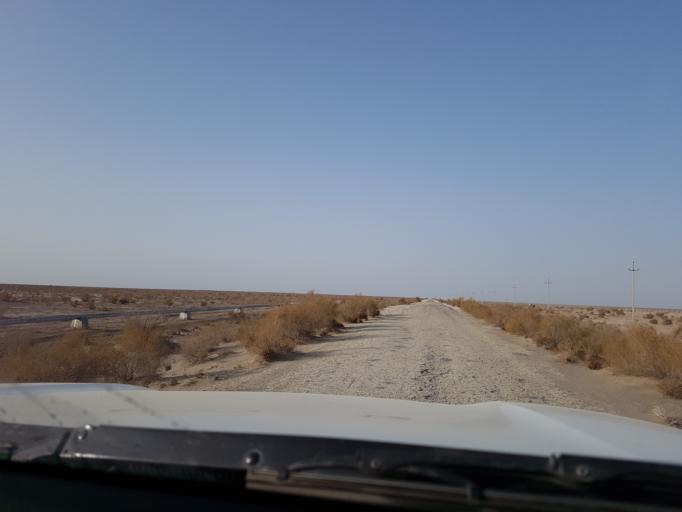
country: UZ
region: Karakalpakstan
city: Shumanay Shahri
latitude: 42.0052
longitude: 58.0762
